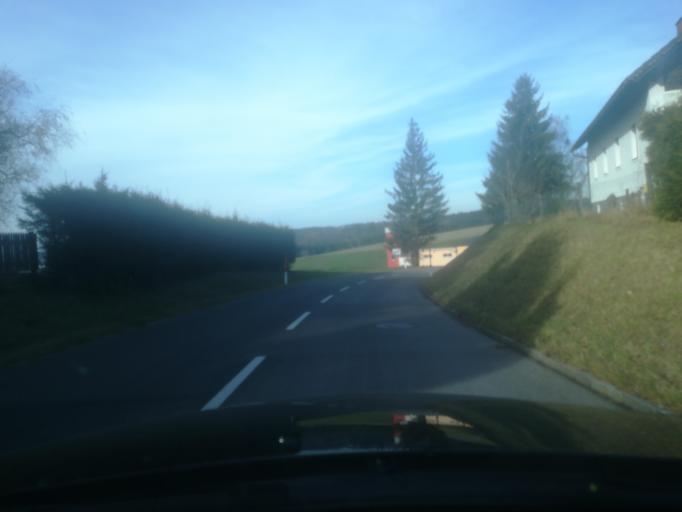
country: AT
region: Upper Austria
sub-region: Politischer Bezirk Perg
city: Perg
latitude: 48.3065
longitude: 14.6595
